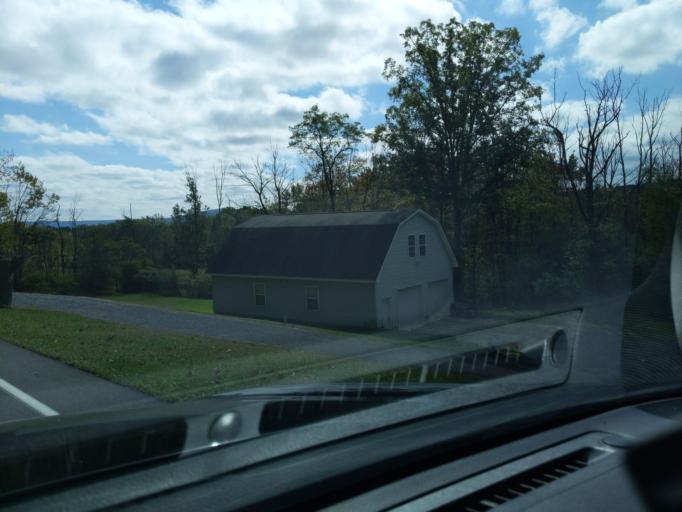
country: US
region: Pennsylvania
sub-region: Blair County
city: Lakemont
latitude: 40.4891
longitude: -78.4361
